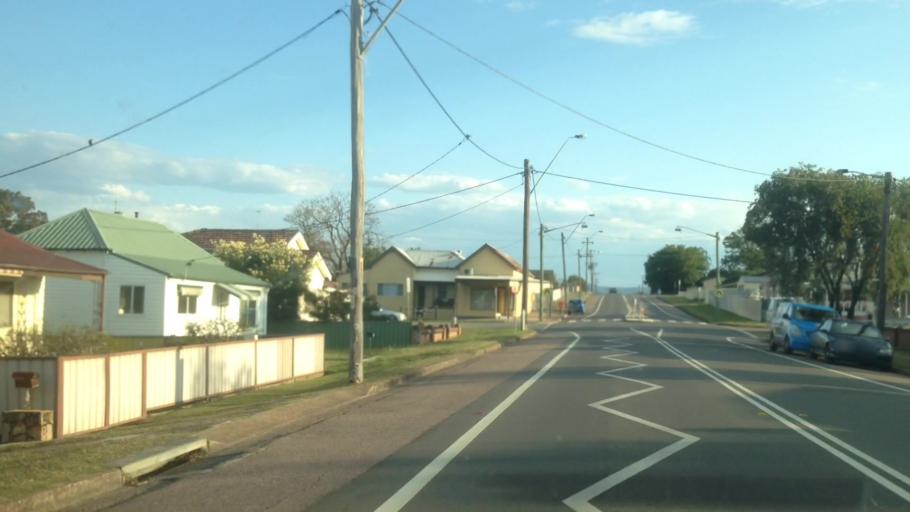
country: AU
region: New South Wales
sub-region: Cessnock
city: Kurri Kurri
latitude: -32.8291
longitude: 151.4814
